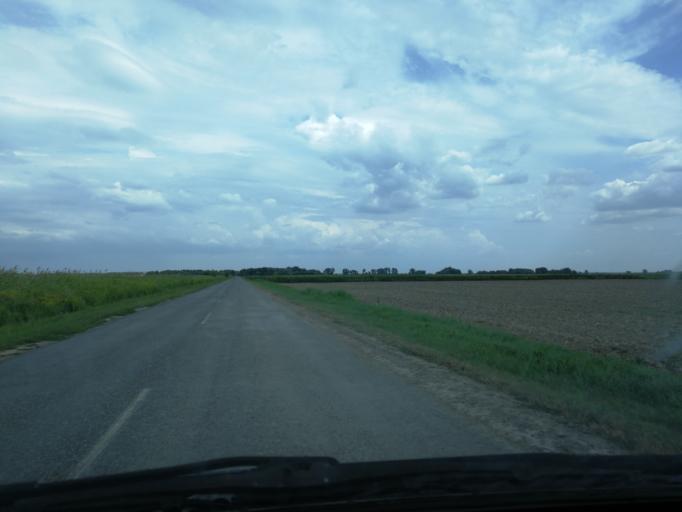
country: HU
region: Bacs-Kiskun
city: Batya
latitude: 46.4455
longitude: 18.9890
